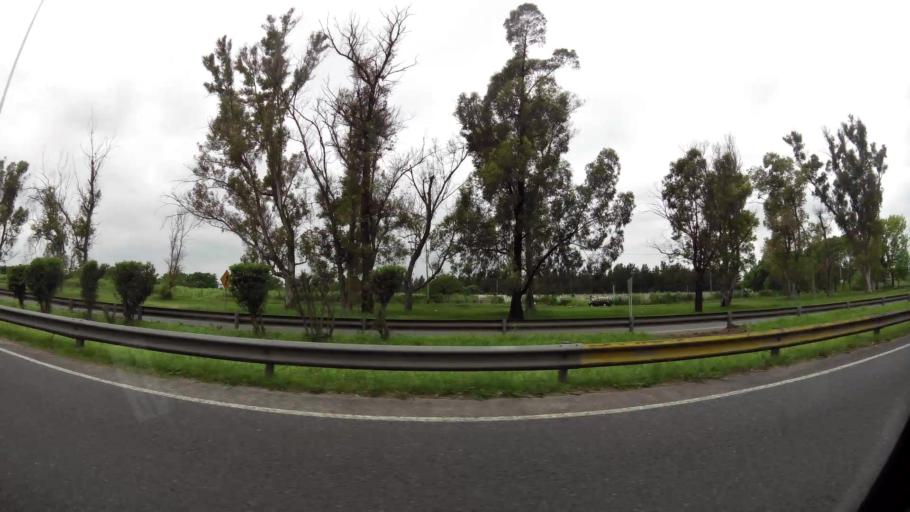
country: AR
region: Buenos Aires
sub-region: Partido de Ezeiza
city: Ezeiza
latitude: -34.8170
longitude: -58.5104
